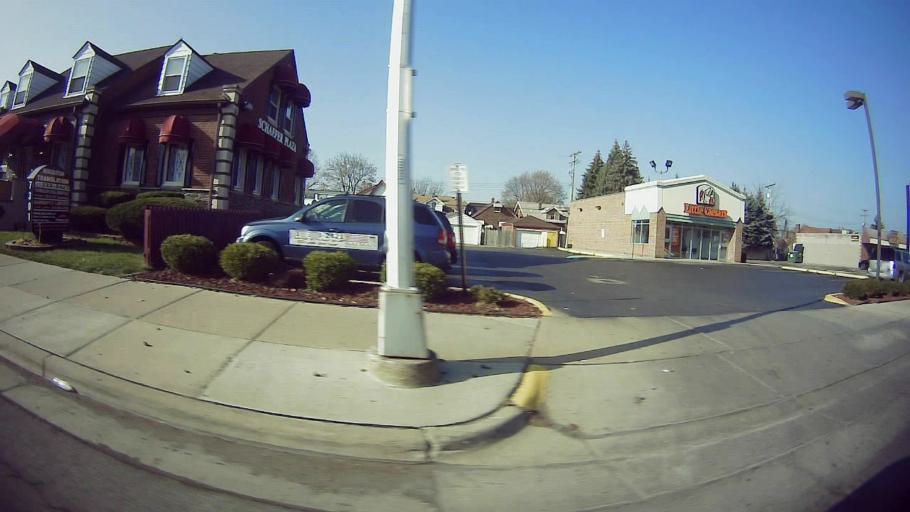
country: US
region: Michigan
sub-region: Wayne County
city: Dearborn
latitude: 42.3448
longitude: -83.1770
